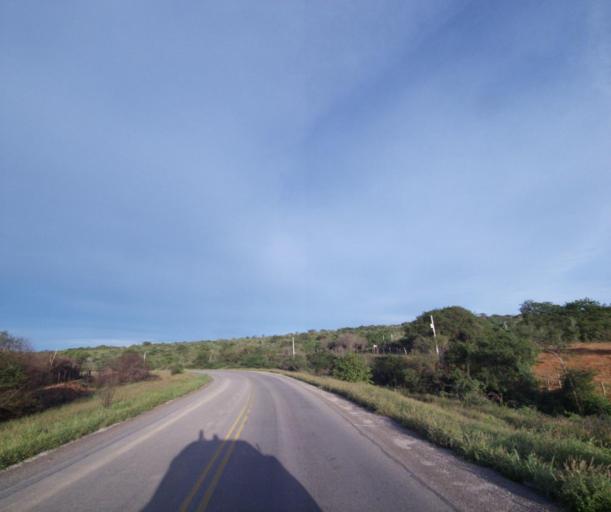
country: BR
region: Bahia
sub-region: Cacule
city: Cacule
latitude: -14.2082
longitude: -42.0656
